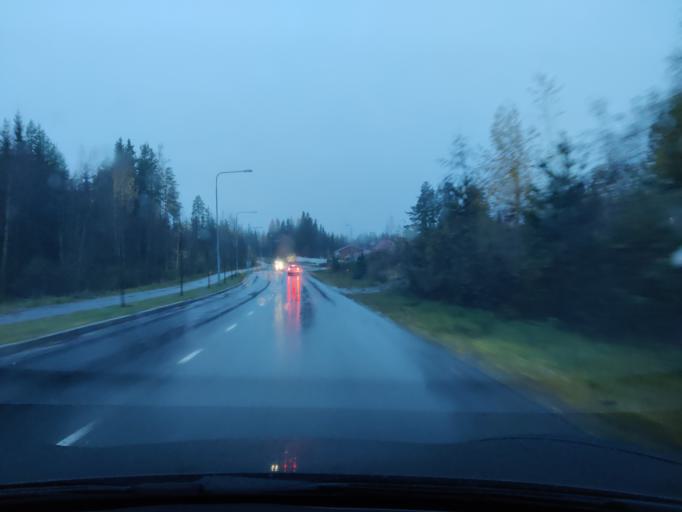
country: FI
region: Northern Savo
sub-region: Kuopio
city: Kuopio
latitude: 62.8311
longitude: 27.7073
